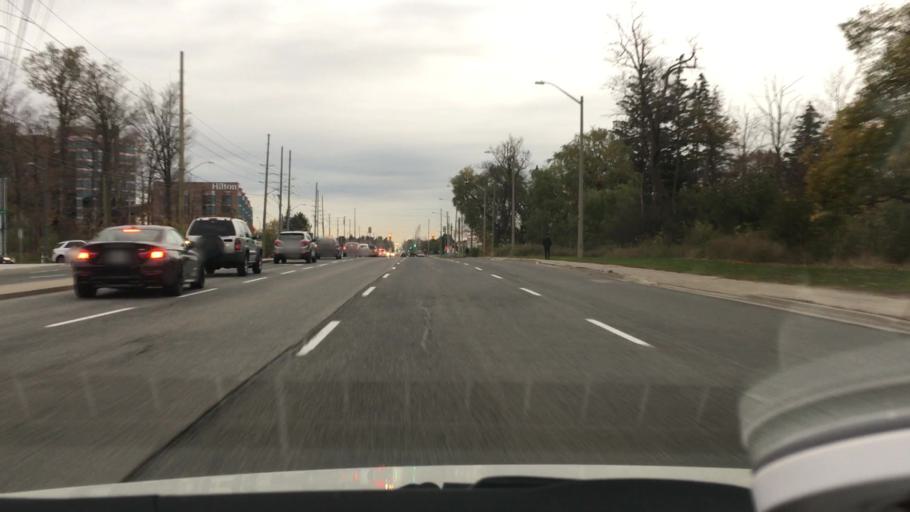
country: CA
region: Ontario
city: Markham
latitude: 43.8518
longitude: -79.3329
